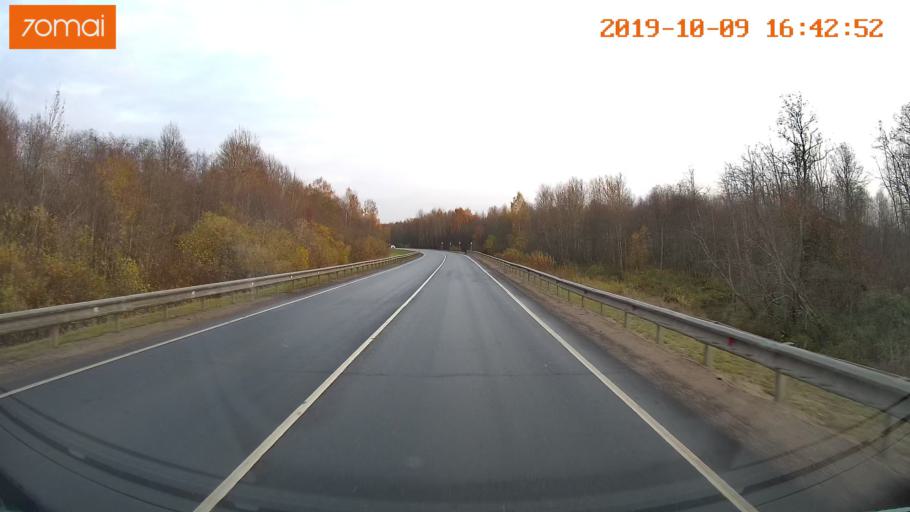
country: RU
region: Kostroma
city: Volgorechensk
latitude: 57.4578
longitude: 41.1092
